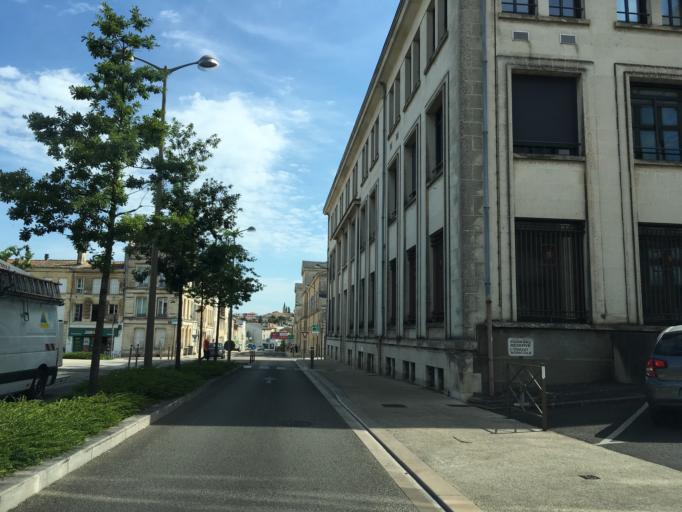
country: FR
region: Poitou-Charentes
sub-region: Departement des Deux-Sevres
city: Niort
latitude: 46.3226
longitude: -0.4565
